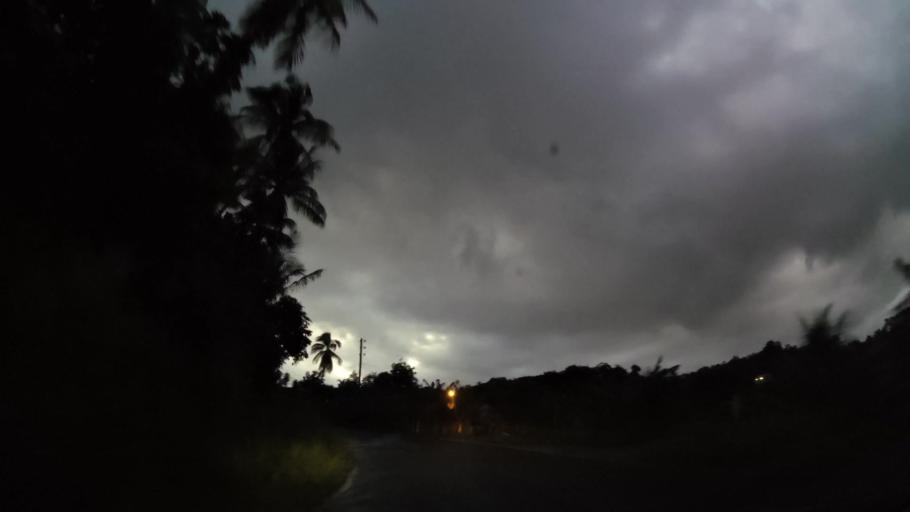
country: DM
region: Saint Andrew
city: Calibishie
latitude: 15.5911
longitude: -61.3413
